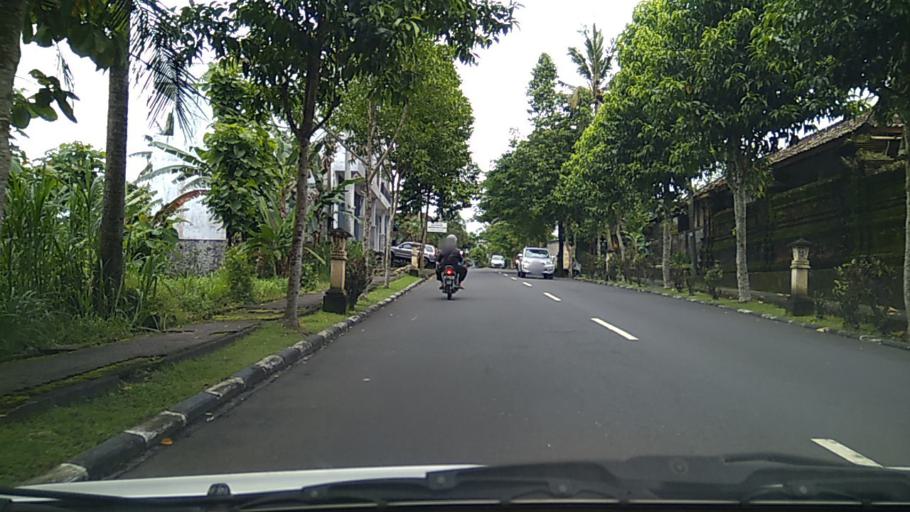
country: ID
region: Bali
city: Banjar Kelodan
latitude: -8.5173
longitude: 115.3458
